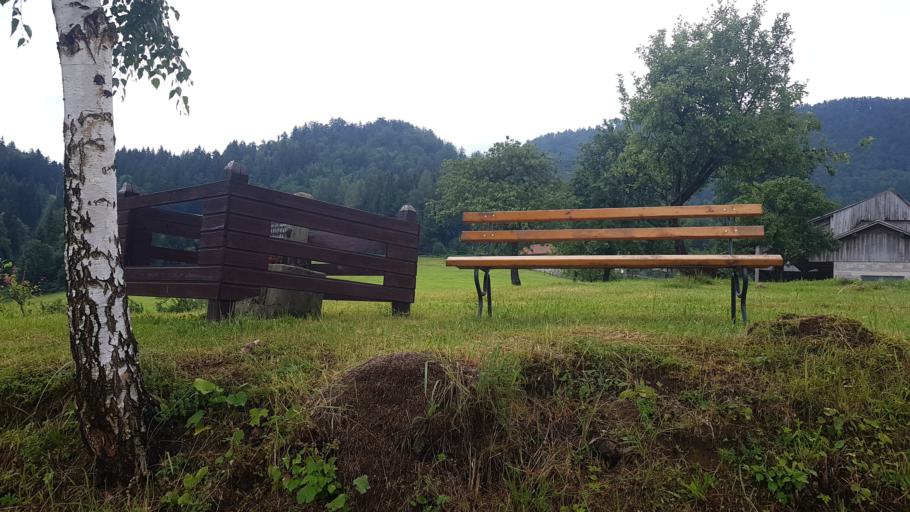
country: SI
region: Recica ob Savinji
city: Recica ob Savinji
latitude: 46.2631
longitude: 14.8865
